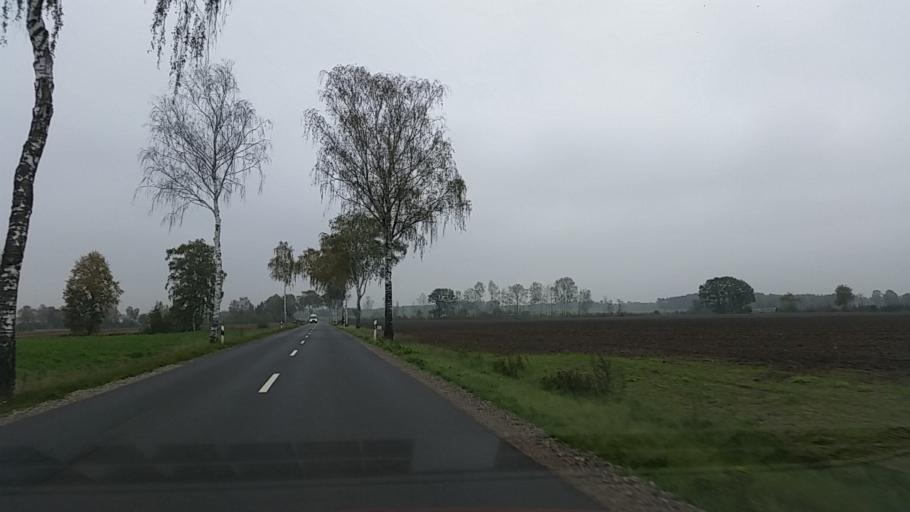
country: DE
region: Lower Saxony
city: Wittingen
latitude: 52.6645
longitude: 10.7006
